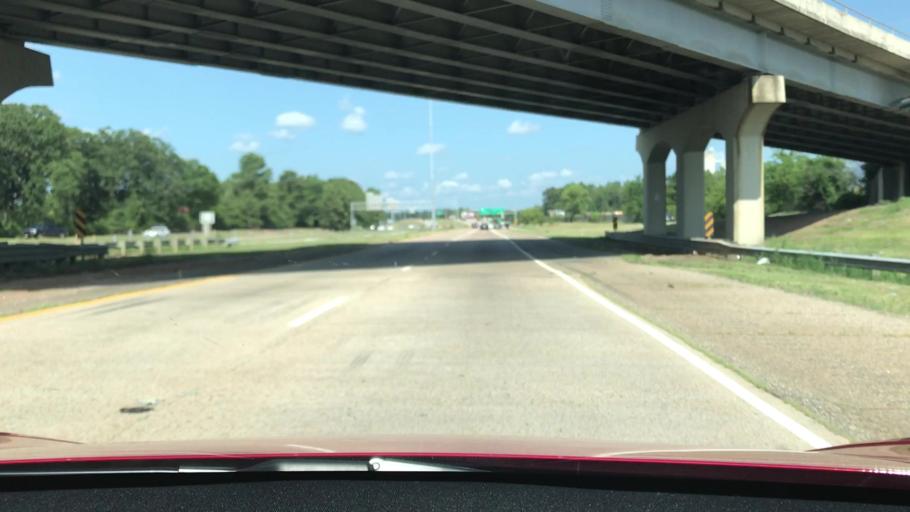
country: US
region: Louisiana
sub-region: Bossier Parish
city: Bossier City
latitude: 32.4198
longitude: -93.7540
